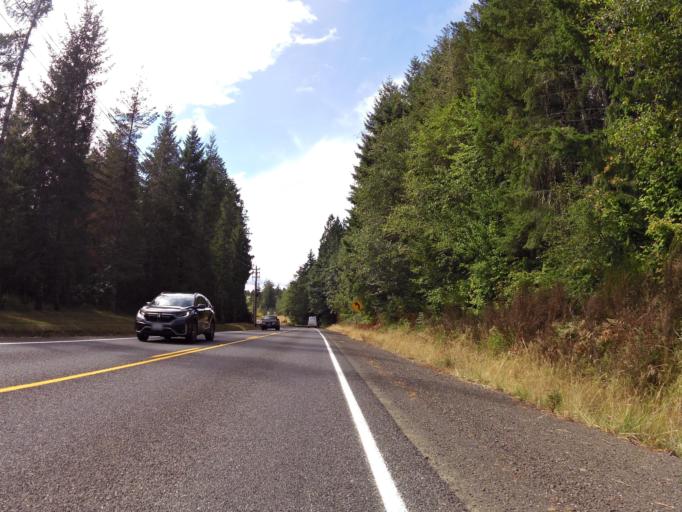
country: US
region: Washington
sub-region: Mason County
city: Shelton
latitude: 47.1562
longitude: -123.0518
